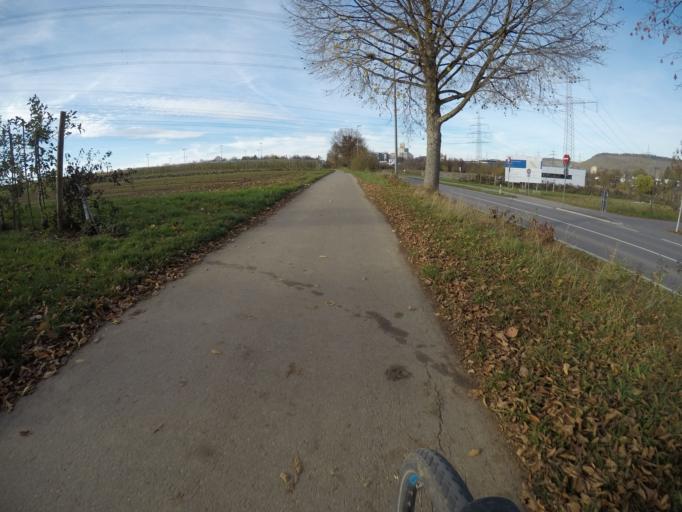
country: DE
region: Baden-Wuerttemberg
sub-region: Regierungsbezirk Stuttgart
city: Weinstadt-Endersbach
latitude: 48.8066
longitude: 9.3808
